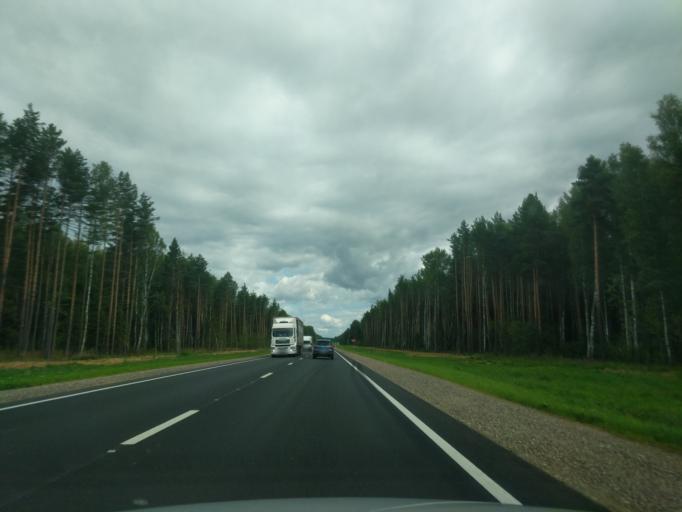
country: RU
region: Jaroslavl
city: Nekrasovskoye
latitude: 57.5821
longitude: 40.2861
